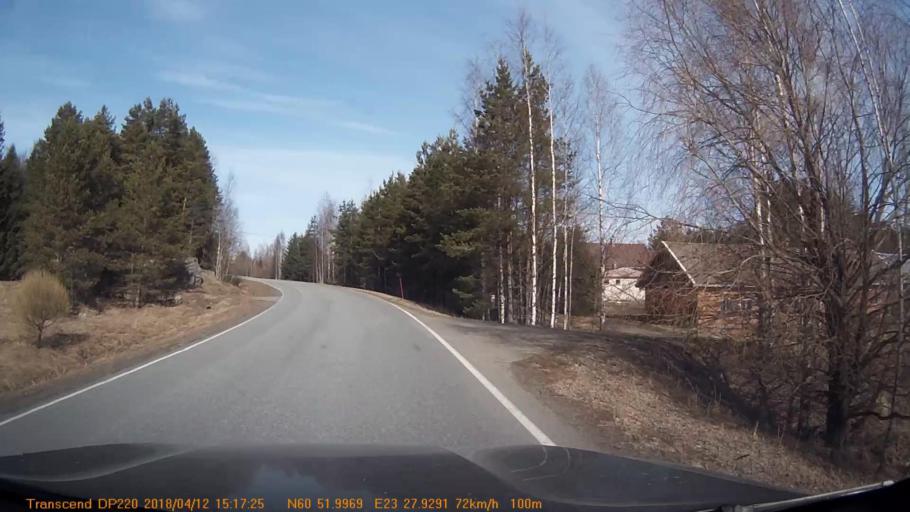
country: FI
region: Haeme
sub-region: Forssa
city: Jokioinen
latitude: 60.8668
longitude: 23.4662
